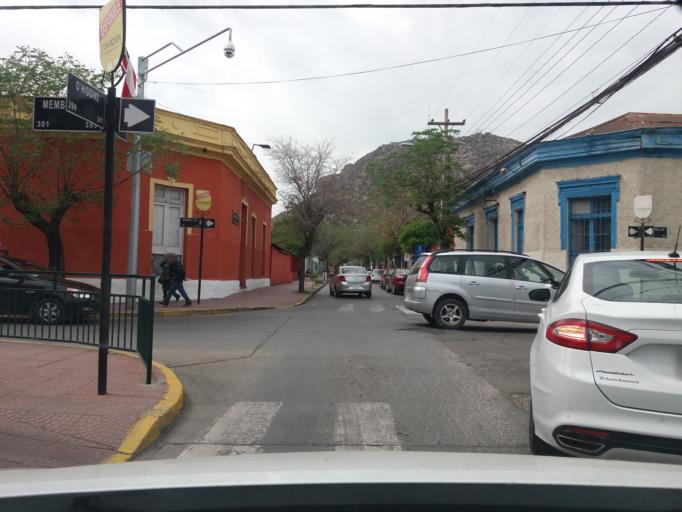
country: CL
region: Valparaiso
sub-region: Provincia de Los Andes
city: Los Andes
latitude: -32.8347
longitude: -70.5966
